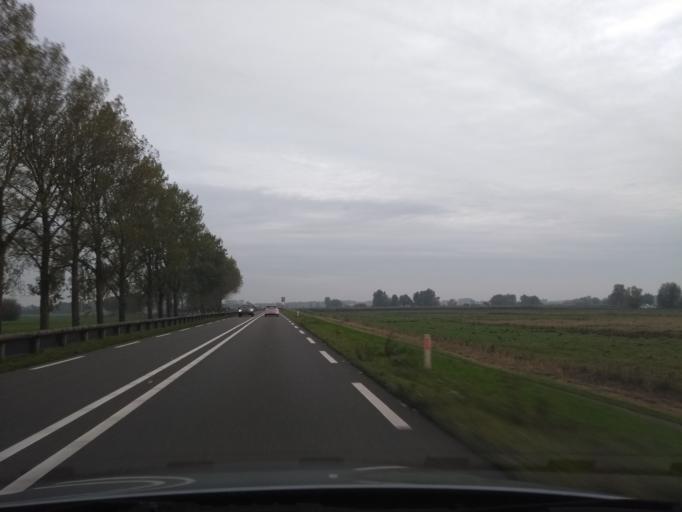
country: NL
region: Overijssel
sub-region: Gemeente Zwartewaterland
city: Hasselt
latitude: 52.6146
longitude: 6.0914
